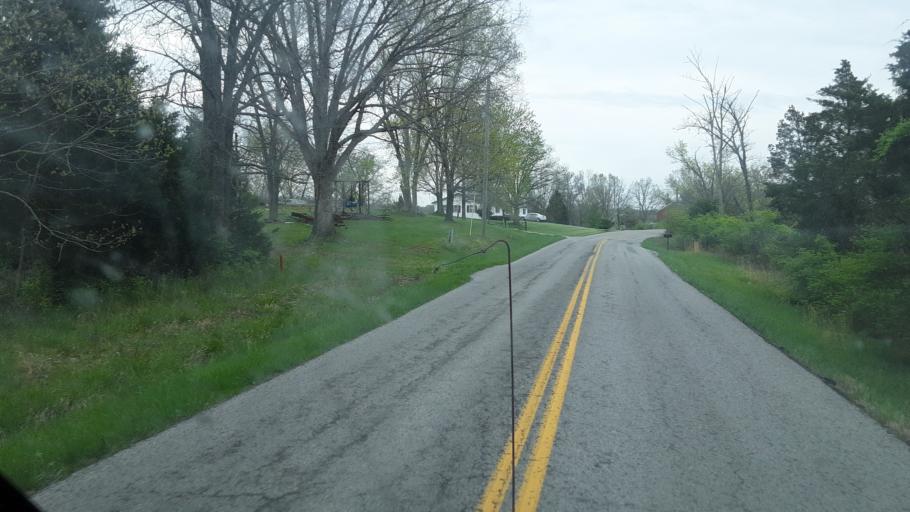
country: US
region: Kentucky
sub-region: Grant County
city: Dry Ridge
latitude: 38.6543
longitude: -84.7027
